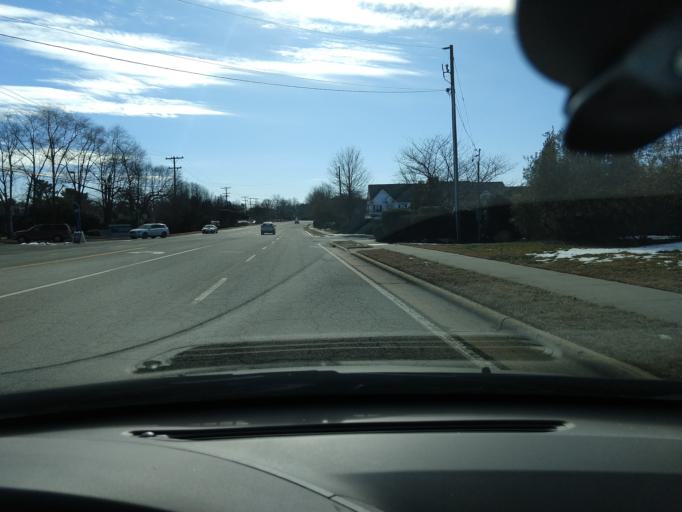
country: US
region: North Carolina
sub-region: Guilford County
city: Oak Ridge
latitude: 36.1150
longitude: -79.9551
